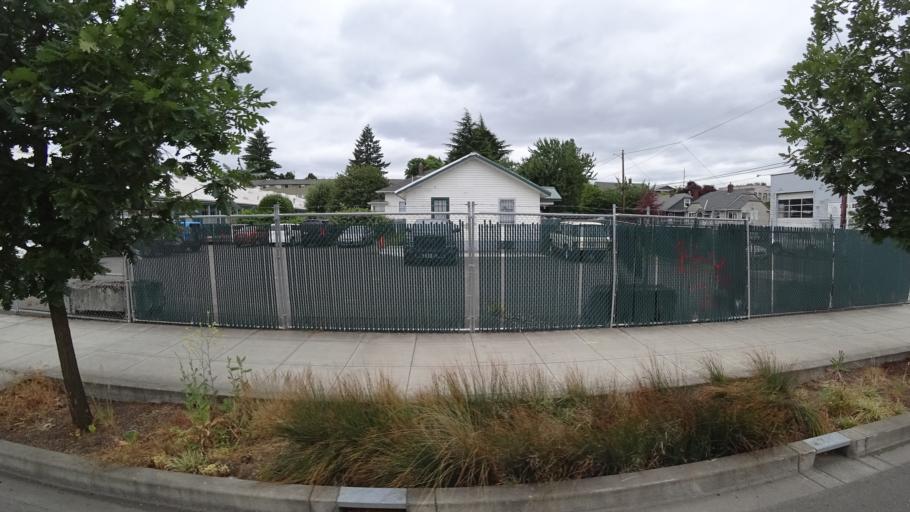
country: US
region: Oregon
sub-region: Multnomah County
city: Portland
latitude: 45.4895
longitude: -122.6487
